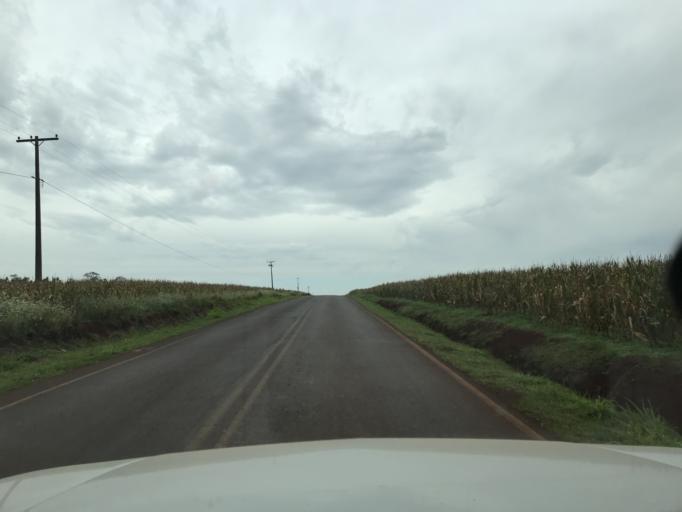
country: BR
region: Parana
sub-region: Marechal Candido Rondon
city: Marechal Candido Rondon
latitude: -24.4502
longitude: -53.9262
